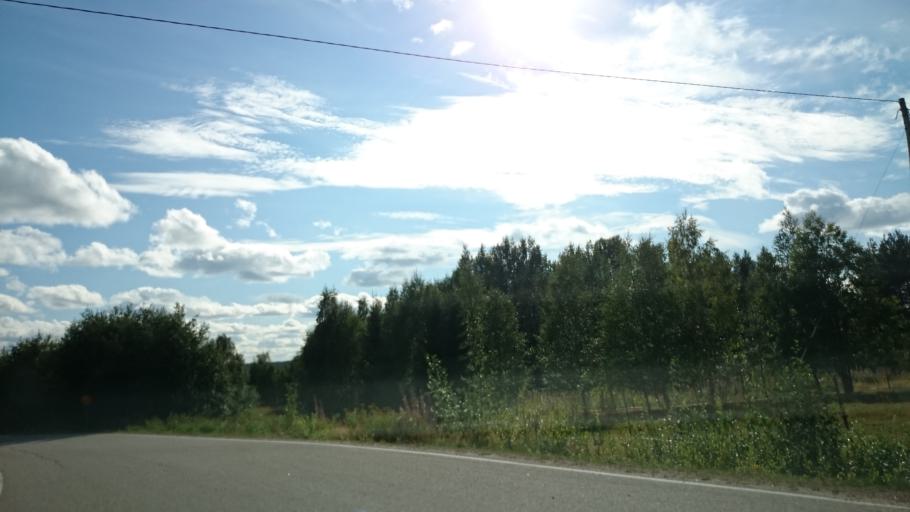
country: FI
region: Kainuu
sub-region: Kehys-Kainuu
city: Suomussalmi
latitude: 64.7470
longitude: 29.4404
